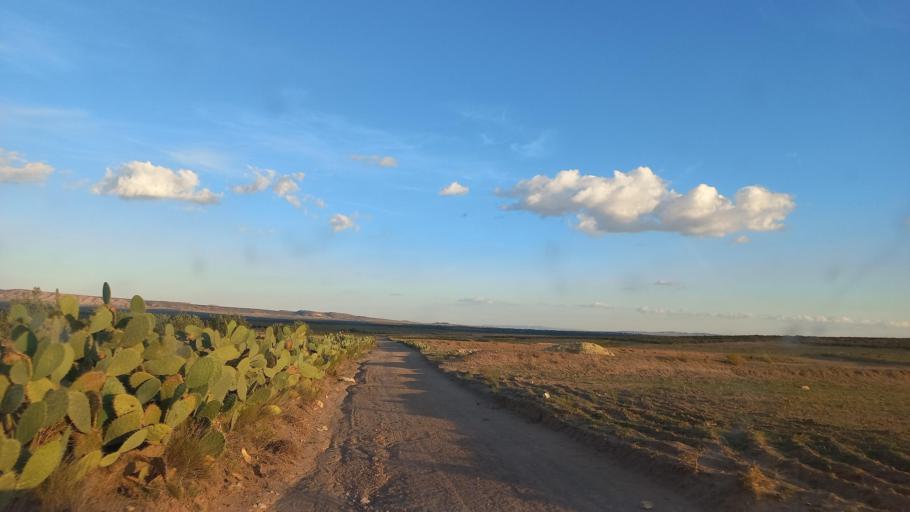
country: TN
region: Al Qasrayn
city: Sbiba
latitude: 35.3515
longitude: 9.0205
